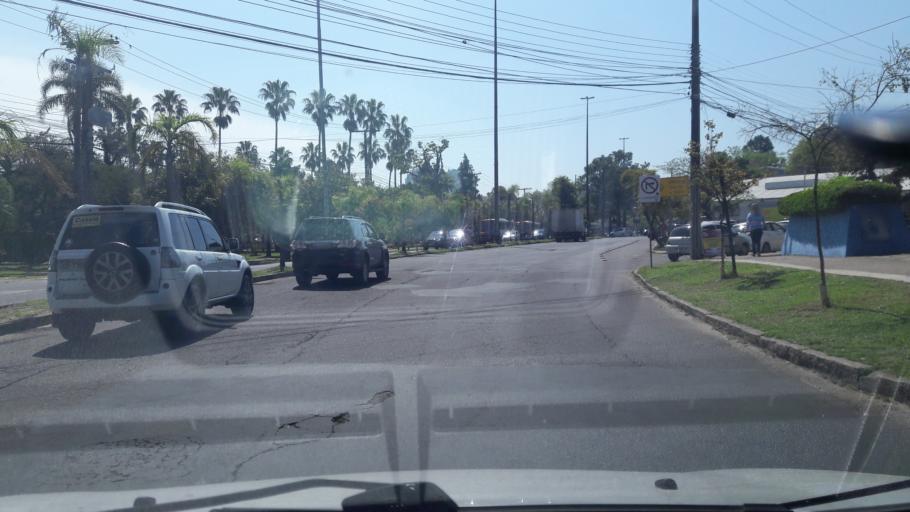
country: BR
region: Rio Grande do Sul
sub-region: Guaiba
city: Guaiba
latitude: -30.1118
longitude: -51.2553
